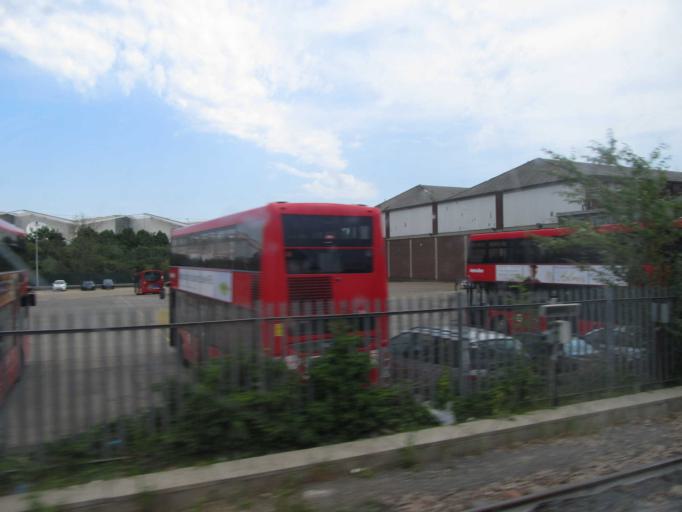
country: GB
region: England
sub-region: Greater London
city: West Drayton
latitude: 51.5069
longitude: -0.4468
